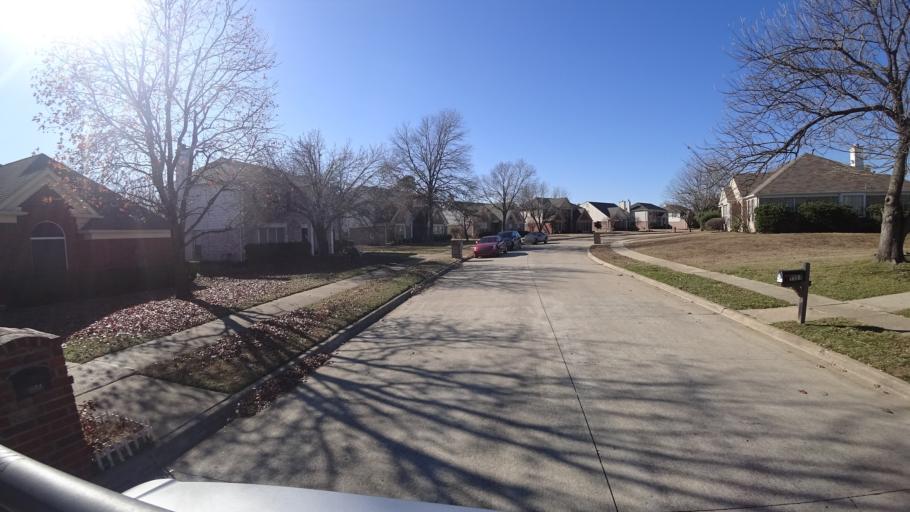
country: US
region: Texas
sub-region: Denton County
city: Lewisville
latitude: 33.0185
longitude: -97.0319
